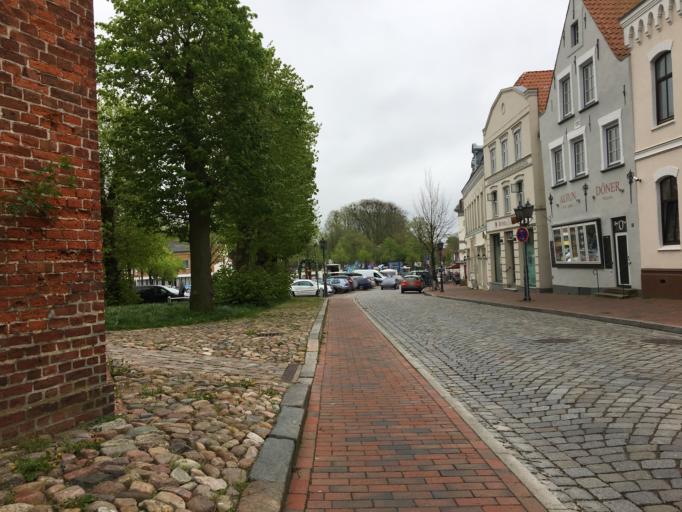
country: DE
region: Schleswig-Holstein
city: Tonning
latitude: 54.3172
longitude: 8.9402
